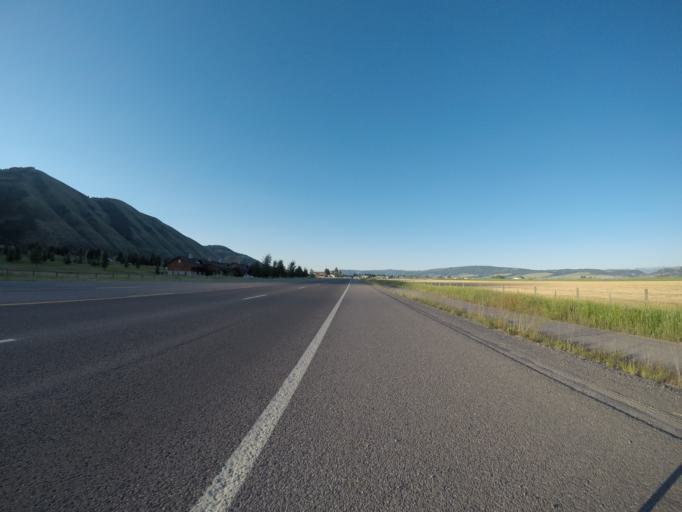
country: US
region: Wyoming
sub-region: Lincoln County
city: Afton
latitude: 42.7052
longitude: -110.9335
